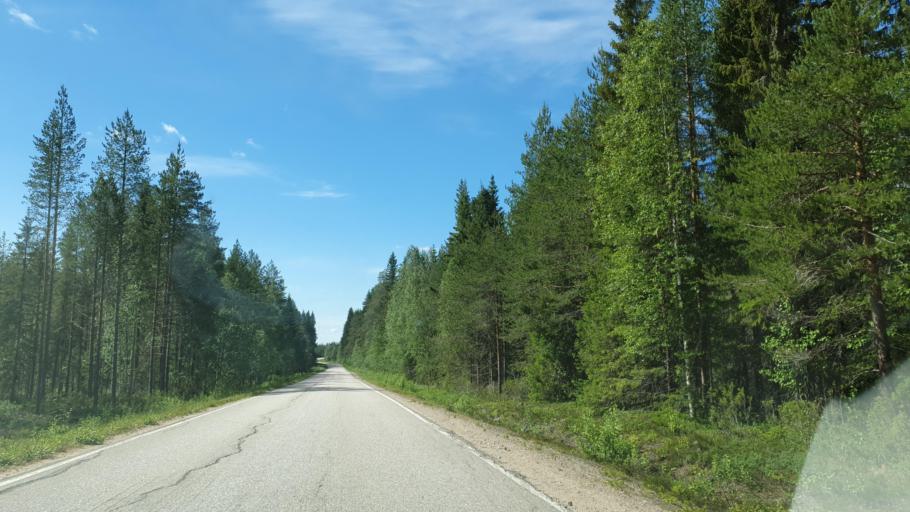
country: FI
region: Kainuu
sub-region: Kehys-Kainuu
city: Suomussalmi
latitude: 64.5783
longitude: 29.0357
